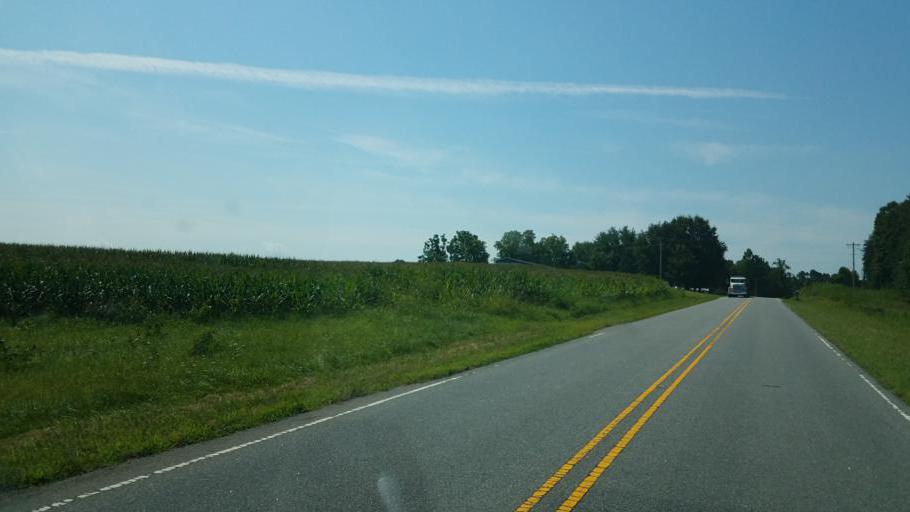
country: US
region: North Carolina
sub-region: Burke County
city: Icard
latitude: 35.5740
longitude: -81.5081
